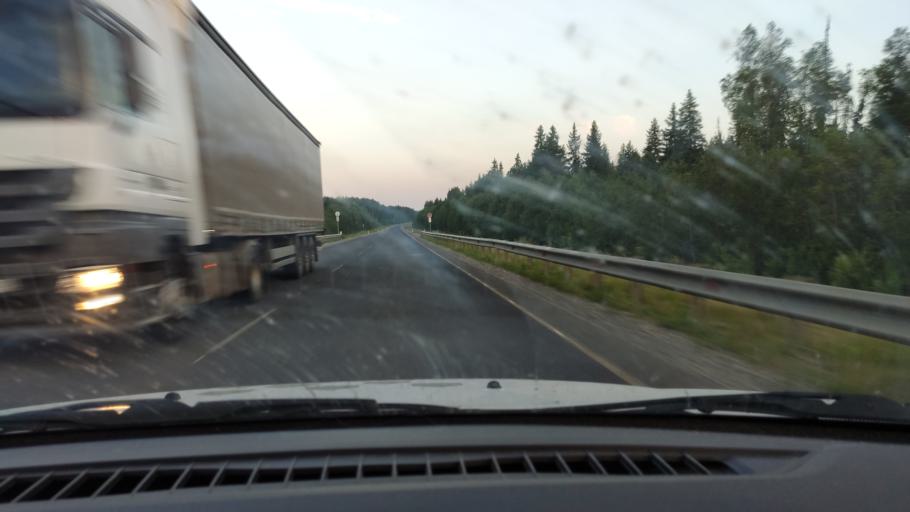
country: RU
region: Perm
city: Siva
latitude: 58.3909
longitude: 54.5424
